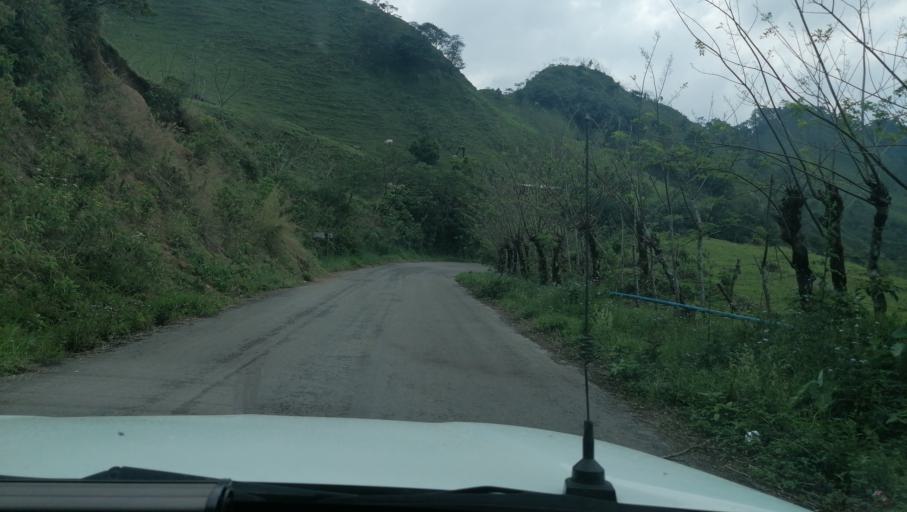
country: MX
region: Chiapas
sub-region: Francisco Leon
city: San Miguel la Sardina
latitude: 17.2379
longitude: -93.3056
